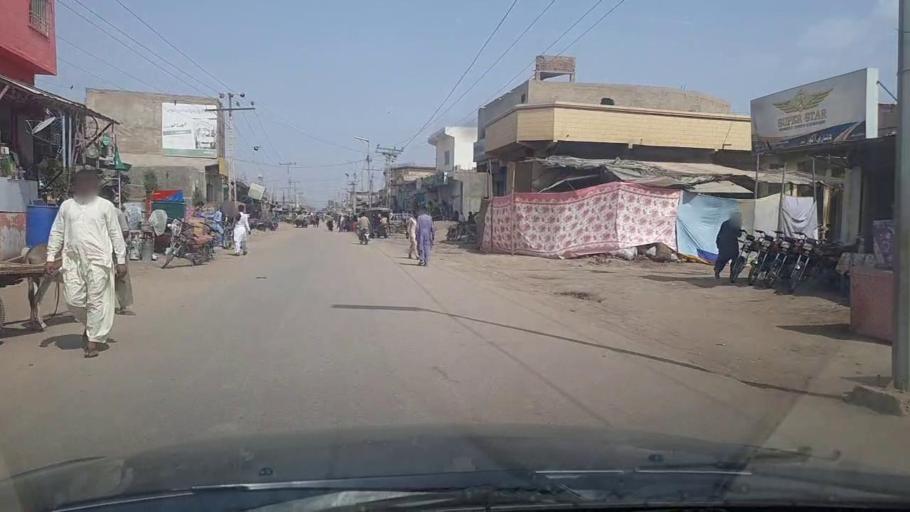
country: PK
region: Sindh
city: Talhar
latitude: 24.8846
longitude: 68.8128
